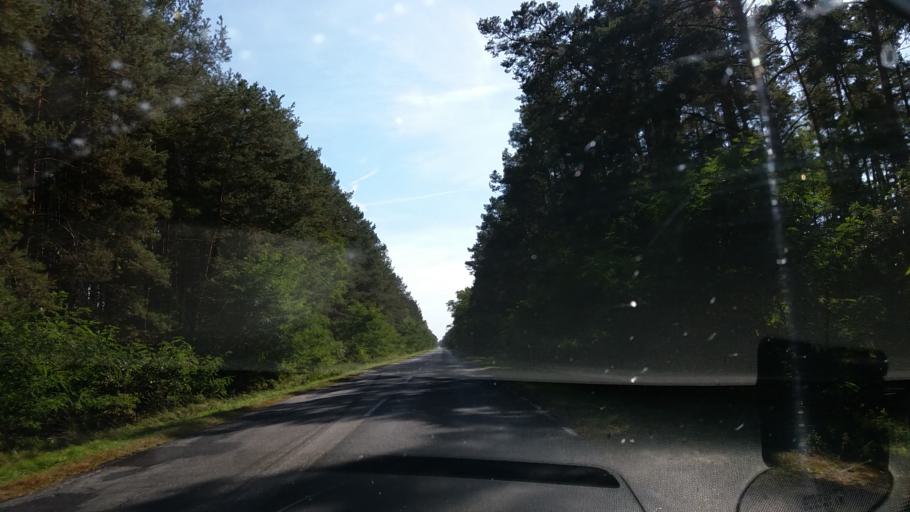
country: PL
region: Lubusz
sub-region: Powiat strzelecko-drezdenecki
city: Drezdenko
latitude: 52.7804
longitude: 15.8419
